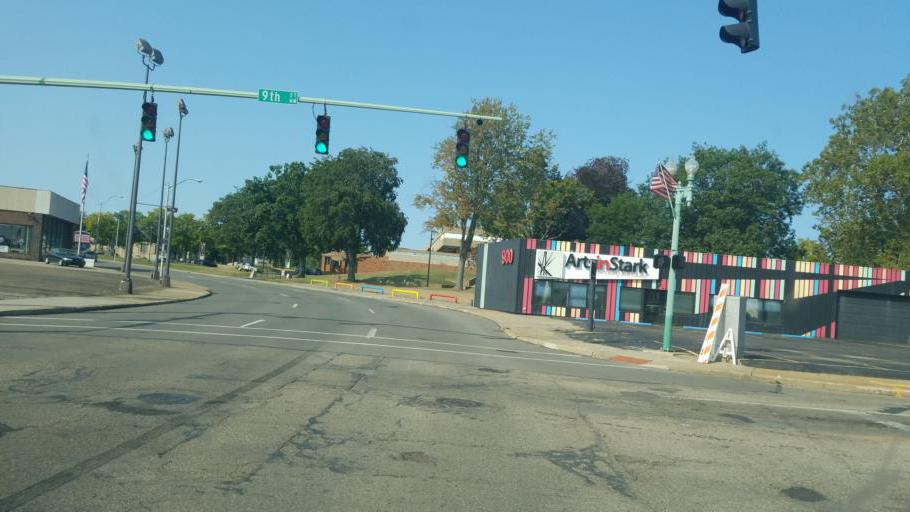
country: US
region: Ohio
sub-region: Stark County
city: Canton
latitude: 40.8052
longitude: -81.3742
